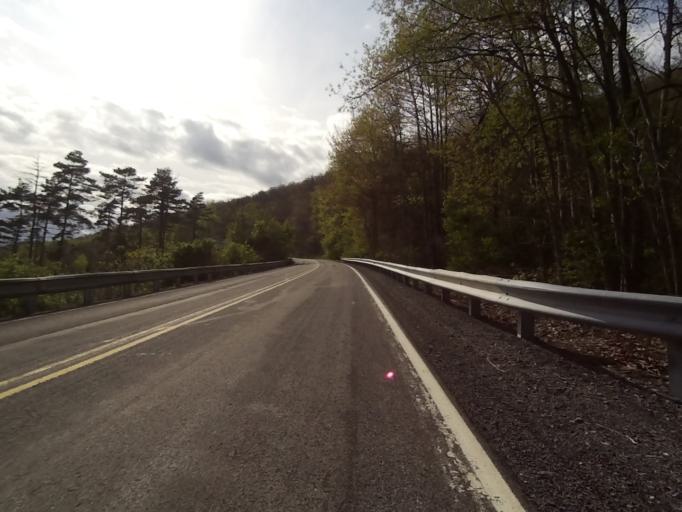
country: US
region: Pennsylvania
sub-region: Centre County
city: Stormstown
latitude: 40.8844
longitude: -77.9951
